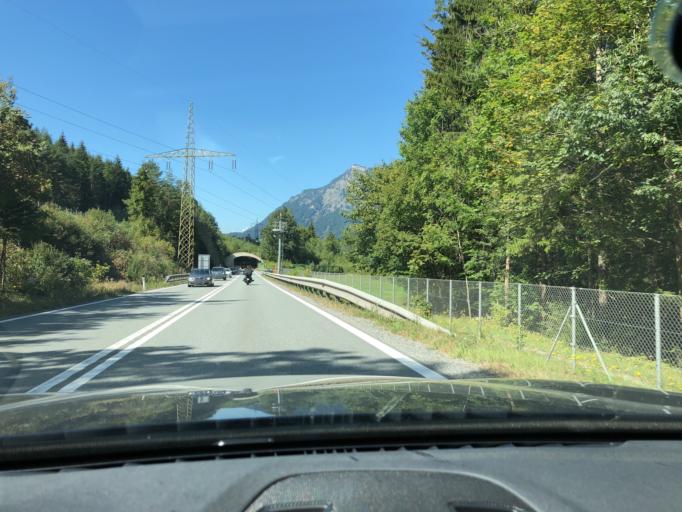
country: AT
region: Vorarlberg
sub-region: Politischer Bezirk Bludenz
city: Innerbraz
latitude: 47.1348
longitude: 9.9438
